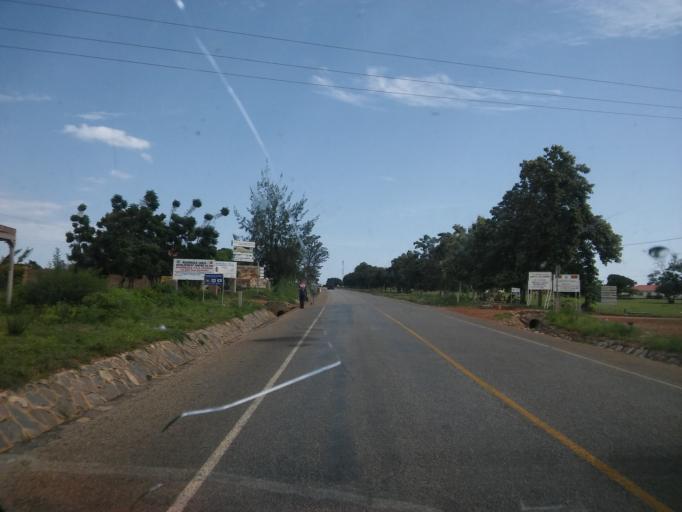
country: UG
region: Eastern Region
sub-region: Bukedea District
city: Bukedea
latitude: 1.3399
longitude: 34.0520
